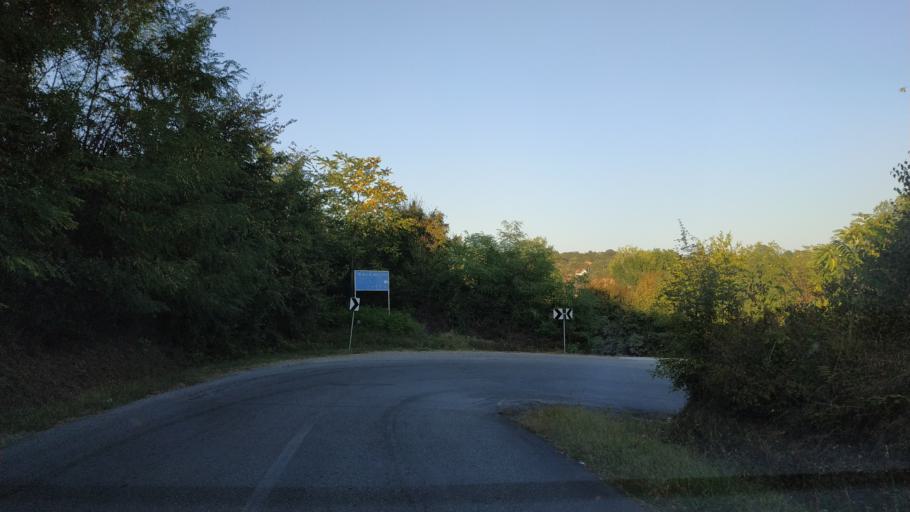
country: RS
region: Central Serbia
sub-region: Sumadijski Okrug
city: Topola
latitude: 44.2652
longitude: 20.6724
